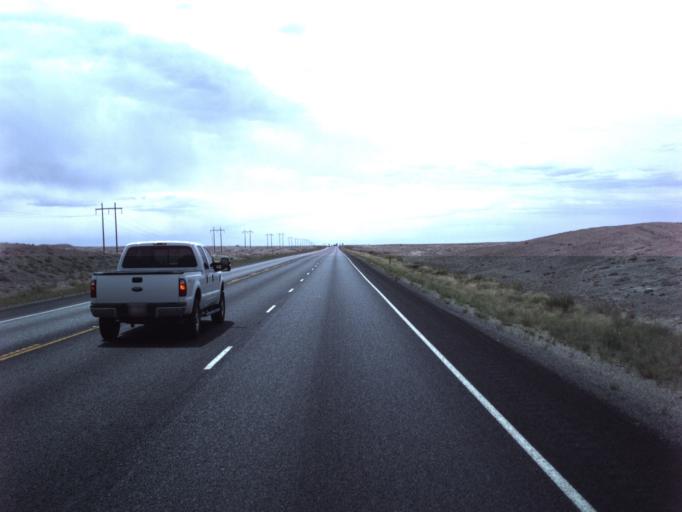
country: US
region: Utah
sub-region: Carbon County
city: East Carbon City
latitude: 39.2073
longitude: -110.3386
